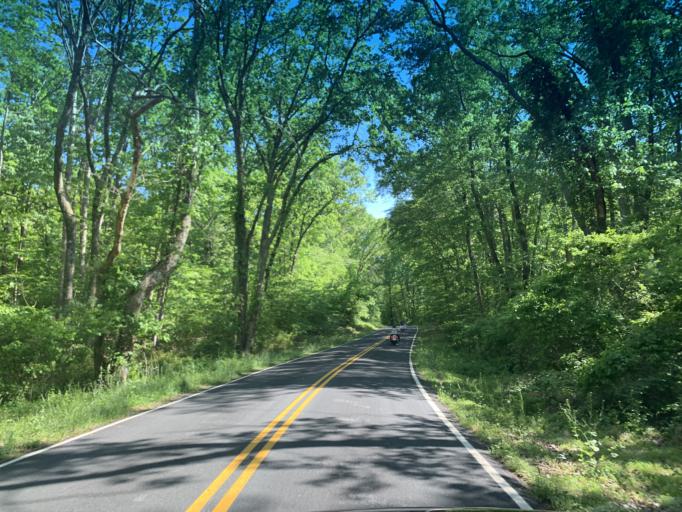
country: US
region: Maryland
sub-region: Cecil County
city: Rising Sun
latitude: 39.6957
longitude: -76.1997
